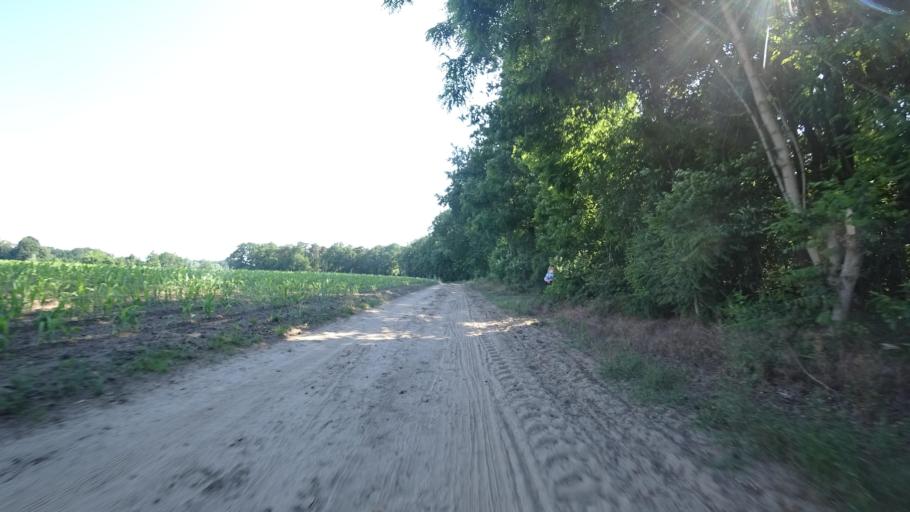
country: DE
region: North Rhine-Westphalia
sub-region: Regierungsbezirk Detmold
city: Guetersloh
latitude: 51.8940
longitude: 8.3343
